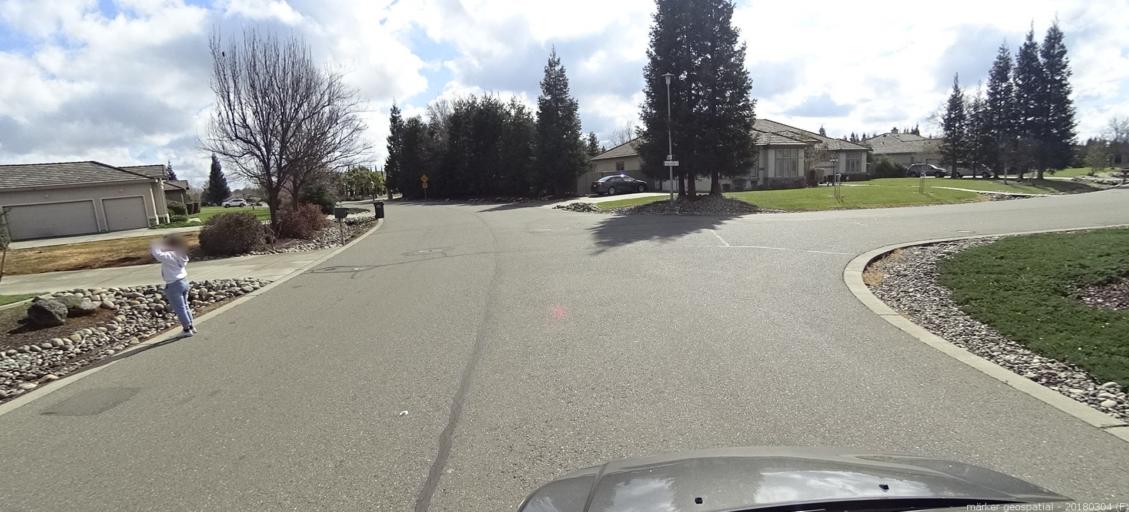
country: US
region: California
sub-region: Sacramento County
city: Vineyard
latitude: 38.4685
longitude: -121.3148
